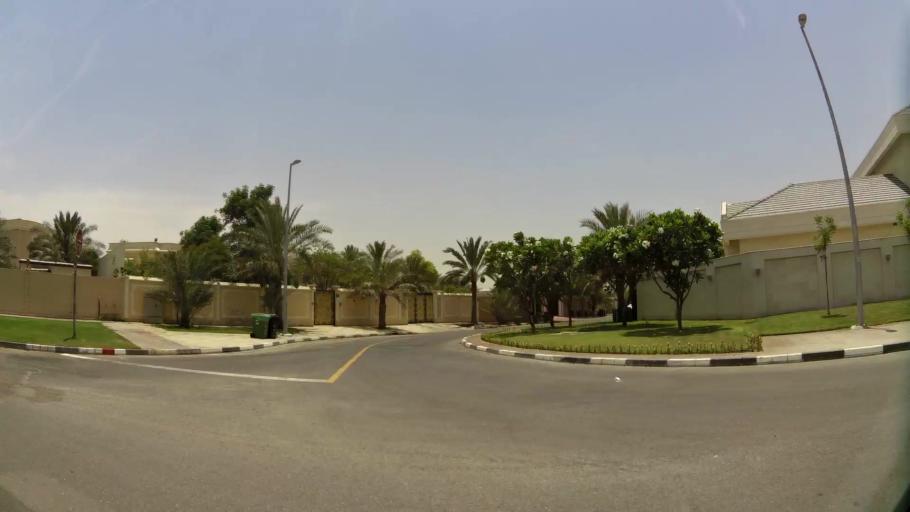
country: AE
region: Ash Shariqah
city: Sharjah
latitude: 25.2461
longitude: 55.4556
